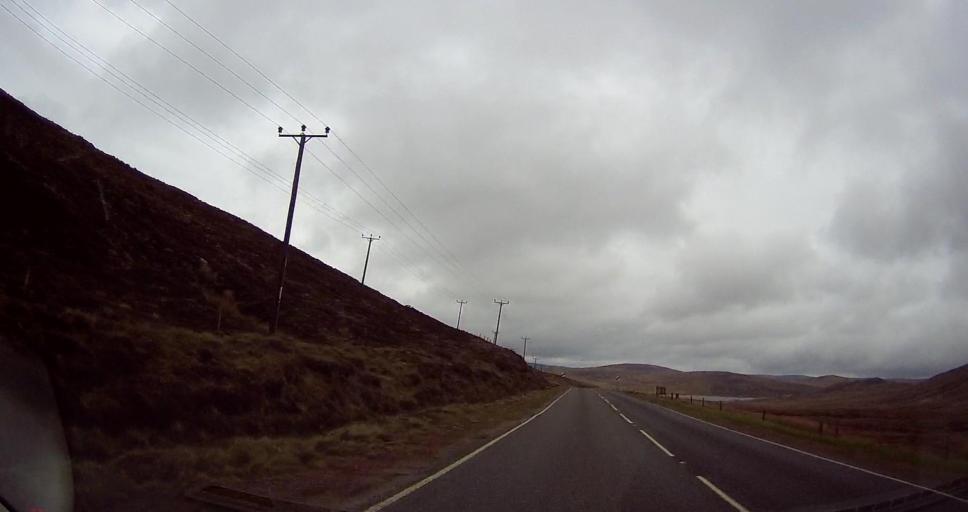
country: GB
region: Scotland
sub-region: Shetland Islands
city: Lerwick
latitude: 60.3306
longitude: -1.2540
